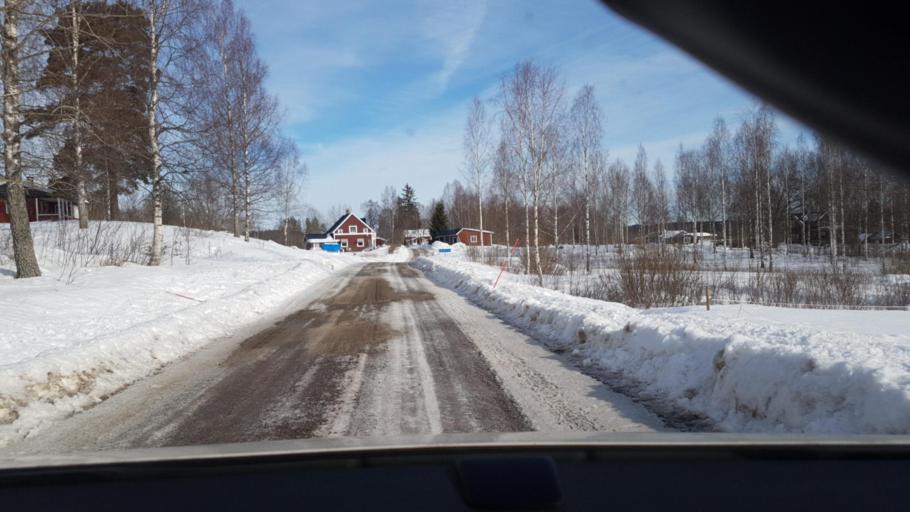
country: NO
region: Ostfold
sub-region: Romskog
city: Romskog
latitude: 59.8599
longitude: 11.9683
